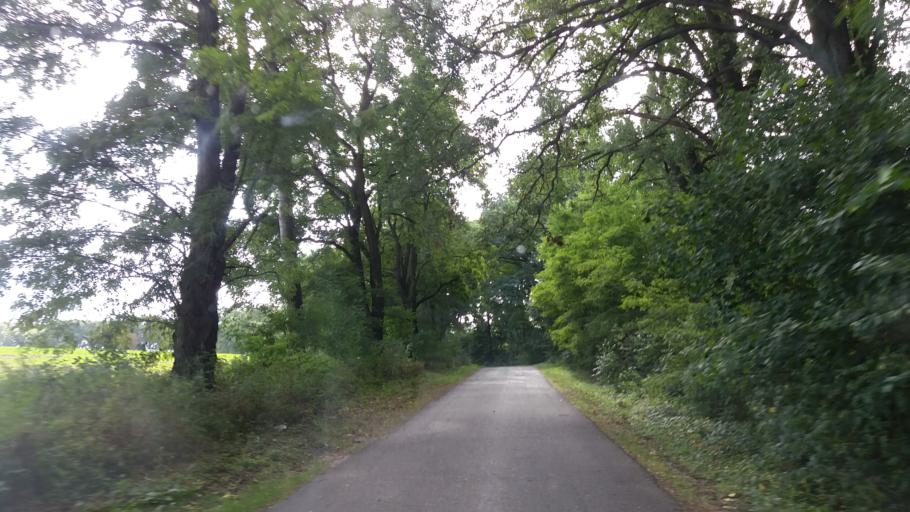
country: PL
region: West Pomeranian Voivodeship
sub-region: Powiat stargardzki
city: Suchan
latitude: 53.2315
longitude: 15.3579
